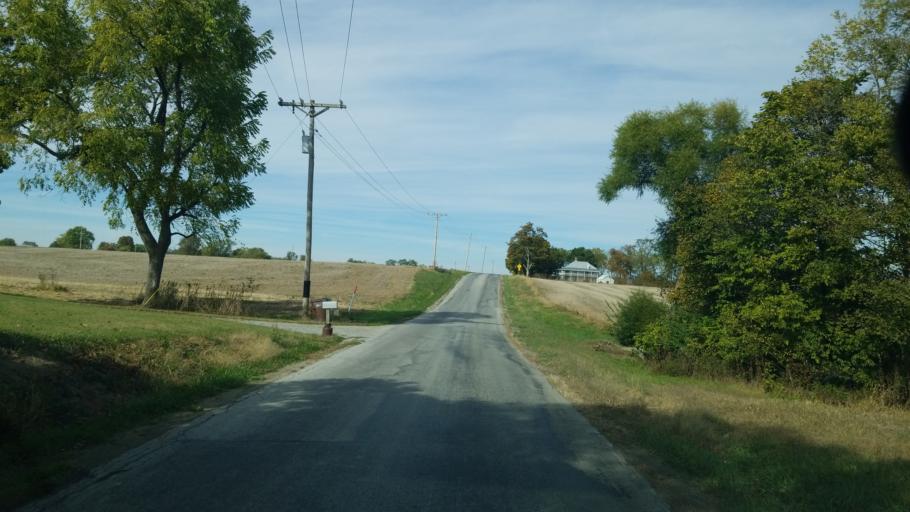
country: US
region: Ohio
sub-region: Highland County
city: Leesburg
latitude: 39.3222
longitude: -83.4730
